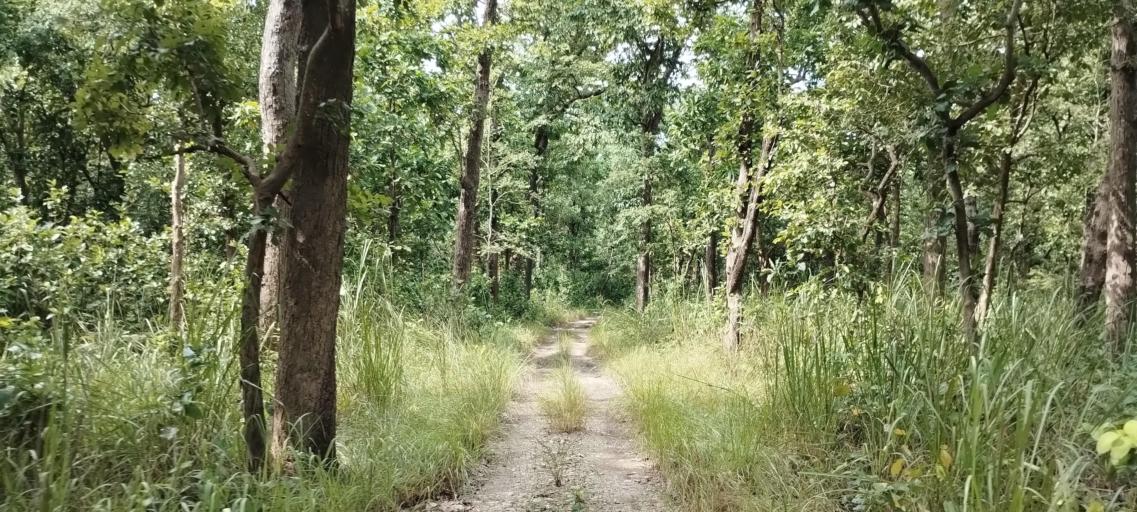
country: NP
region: Far Western
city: Tikapur
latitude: 28.5330
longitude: 81.2832
